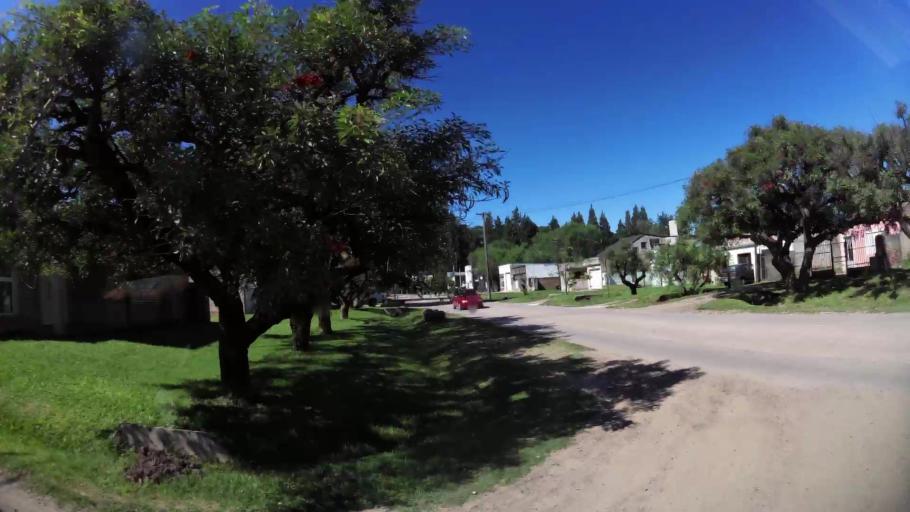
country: AR
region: Santa Fe
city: Esperanza
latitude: -31.4680
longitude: -60.9382
